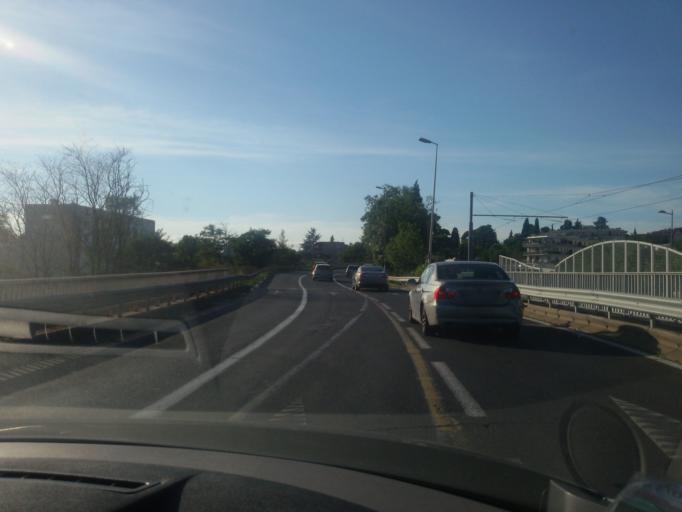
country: FR
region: Languedoc-Roussillon
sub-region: Departement de l'Herault
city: Montpellier
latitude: 43.5959
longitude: 3.8774
